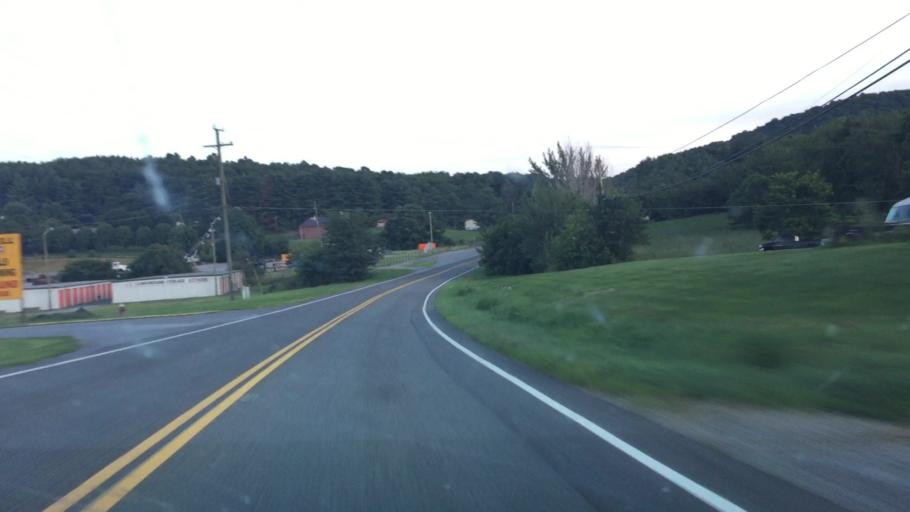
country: US
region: Virginia
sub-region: Wythe County
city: Wytheville
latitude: 36.9403
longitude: -80.9440
